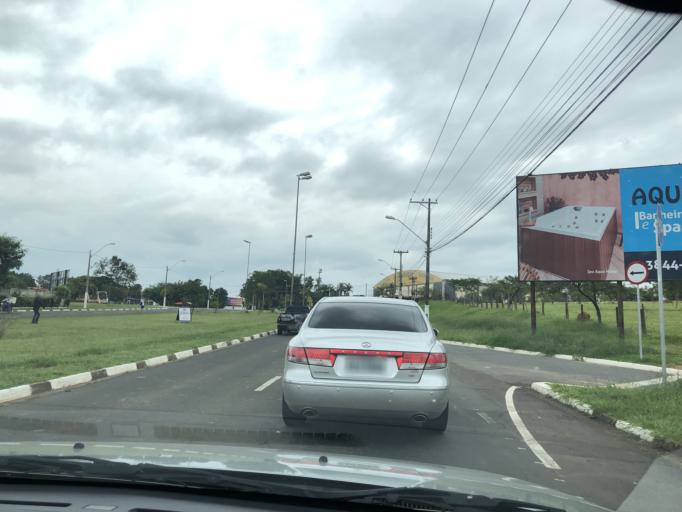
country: BR
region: Sao Paulo
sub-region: Paulinia
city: Paulinia
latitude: -22.7384
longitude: -47.1741
